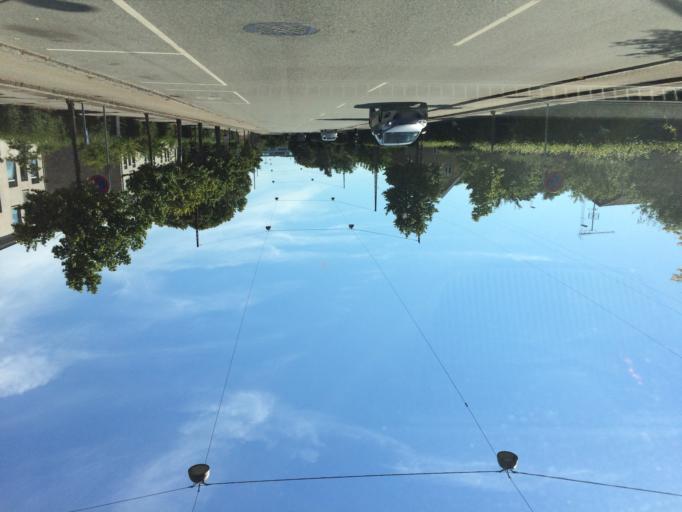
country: DK
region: Capital Region
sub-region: Tarnby Kommune
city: Tarnby
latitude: 55.6340
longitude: 12.6372
